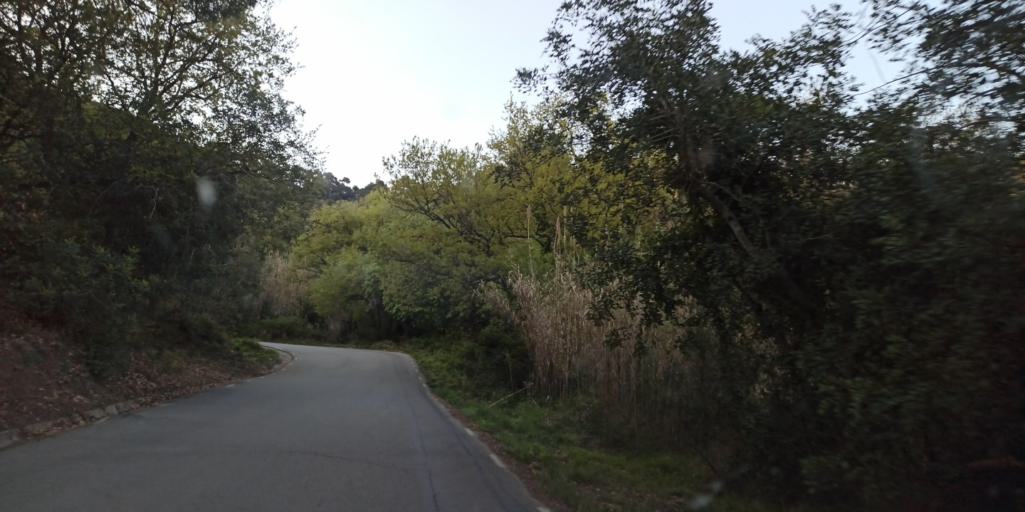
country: ES
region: Catalonia
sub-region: Provincia de Barcelona
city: Sant Just Desvern
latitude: 41.4056
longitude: 2.0878
